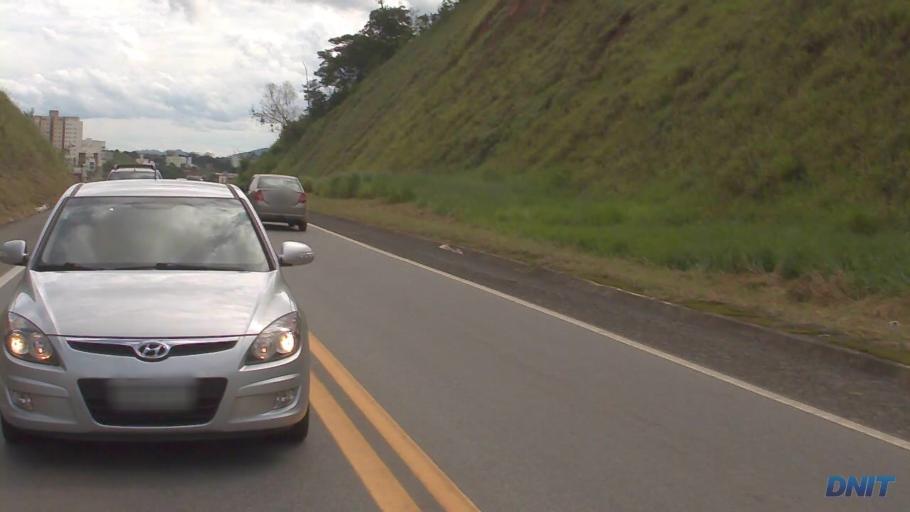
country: BR
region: Minas Gerais
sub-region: Ipatinga
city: Ipatinga
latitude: -19.4504
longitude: -42.5174
